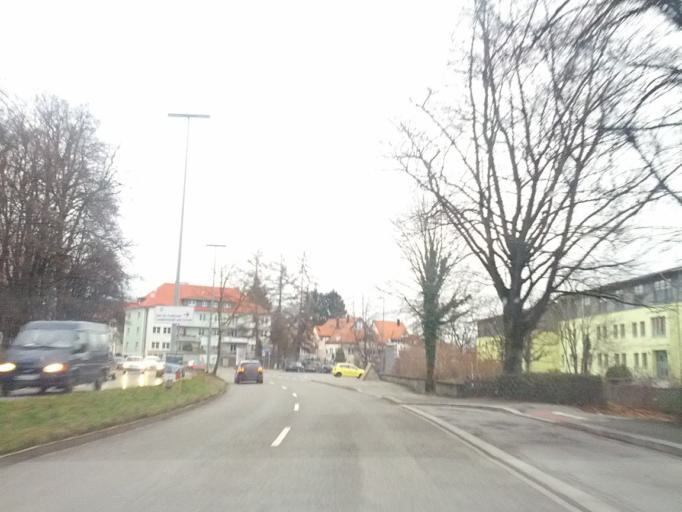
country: DE
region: Bavaria
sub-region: Swabia
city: Kempten (Allgaeu)
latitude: 47.7255
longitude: 10.3042
